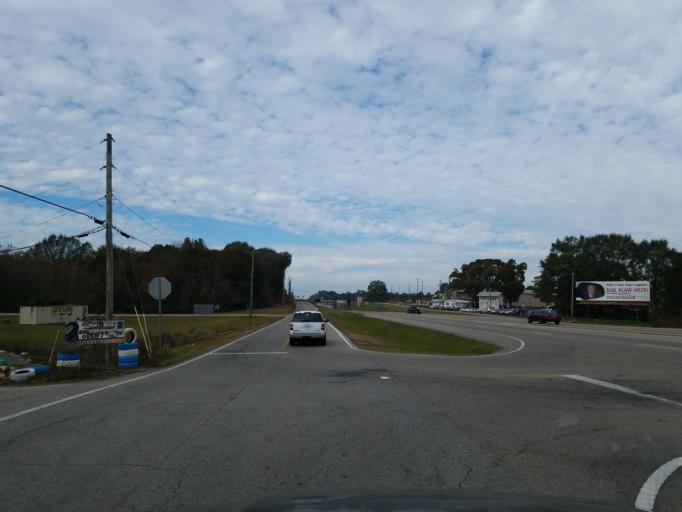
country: US
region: Mississippi
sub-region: Forrest County
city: Hattiesburg
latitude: 31.3009
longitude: -89.3103
